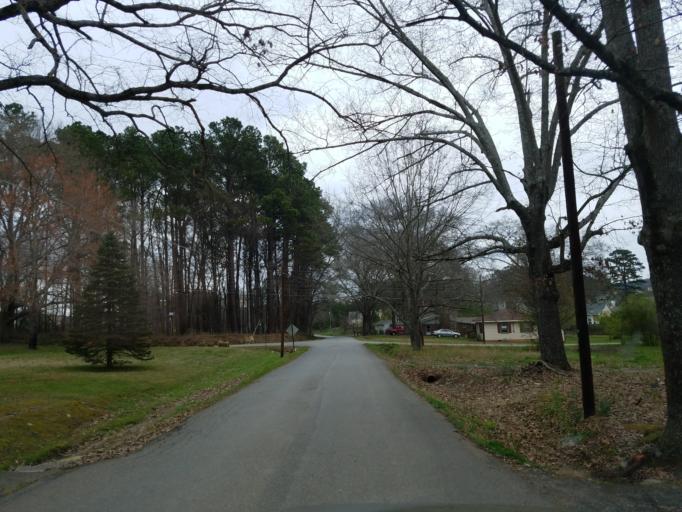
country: US
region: Georgia
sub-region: Bartow County
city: Cartersville
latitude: 34.2130
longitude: -84.7933
